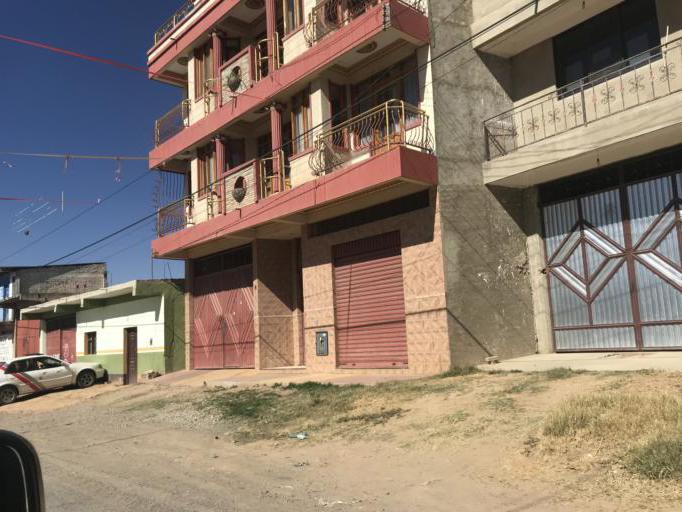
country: BO
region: Cochabamba
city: Cliza
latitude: -17.5890
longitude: -65.9259
